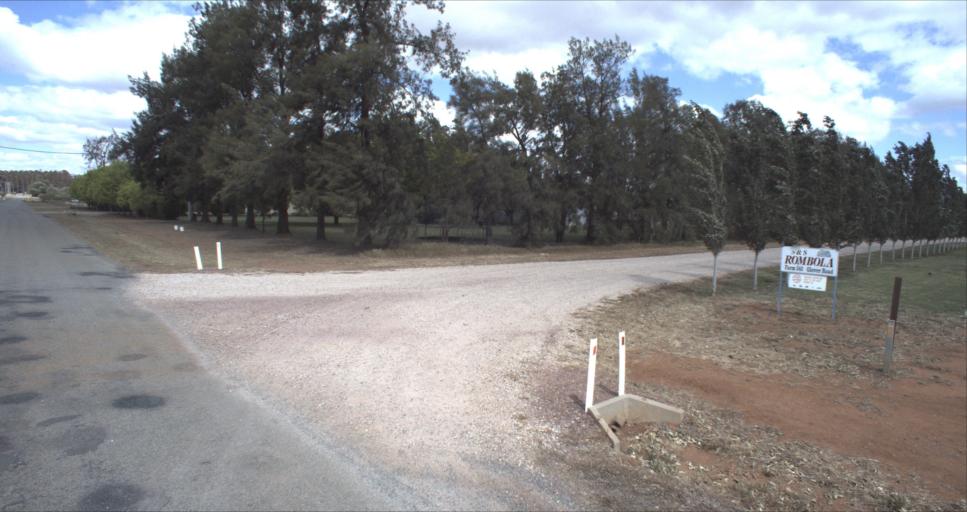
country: AU
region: New South Wales
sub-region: Leeton
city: Leeton
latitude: -34.5811
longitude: 146.4088
